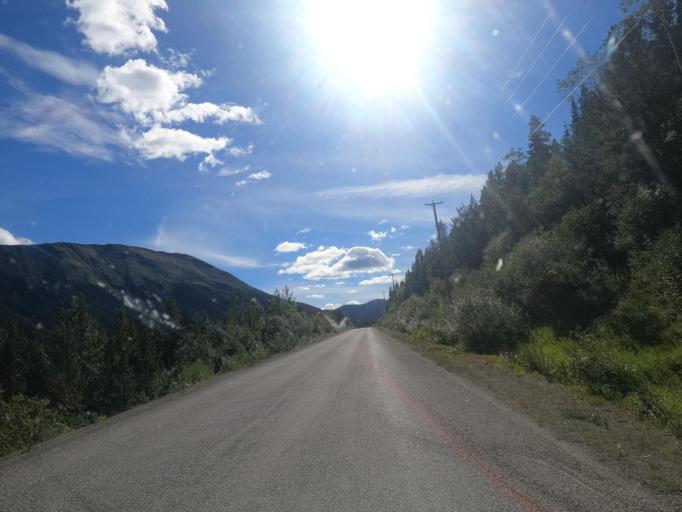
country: CA
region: Yukon
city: Watson Lake
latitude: 59.2825
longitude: -129.5446
